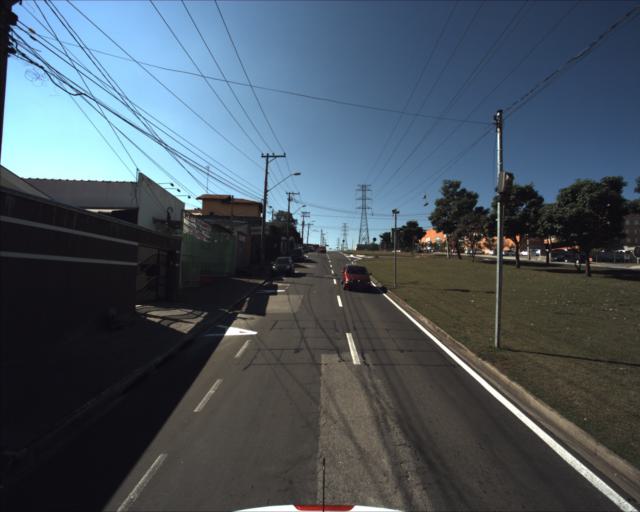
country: BR
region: Sao Paulo
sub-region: Sorocaba
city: Sorocaba
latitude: -23.5141
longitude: -47.4934
